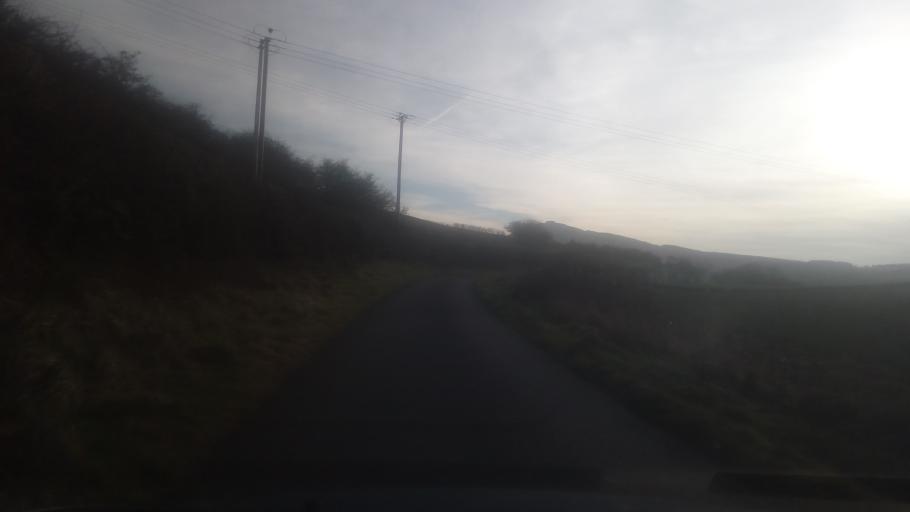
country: GB
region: Scotland
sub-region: The Scottish Borders
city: Jedburgh
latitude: 55.4630
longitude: -2.6334
